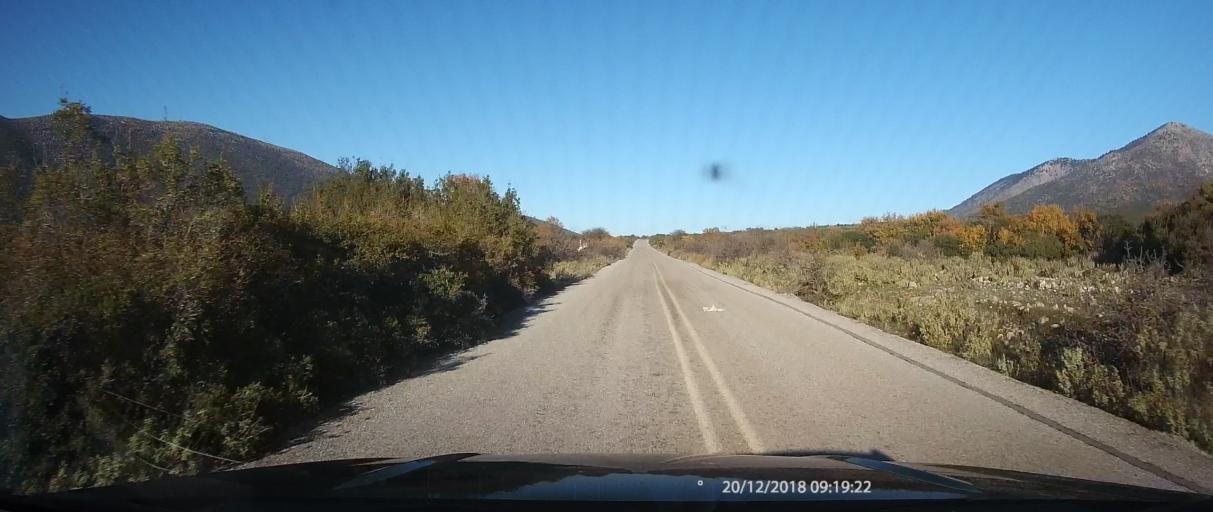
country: GR
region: Peloponnese
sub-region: Nomos Lakonias
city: Molaoi
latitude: 36.9180
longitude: 22.9412
